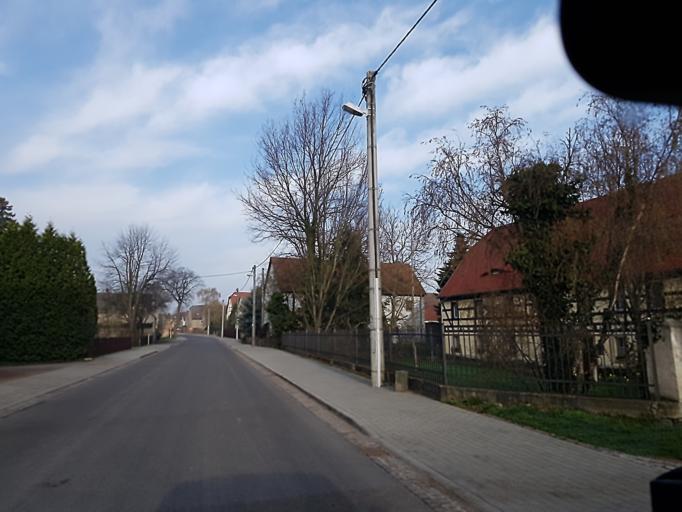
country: DE
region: Saxony
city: Naundorf
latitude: 51.2569
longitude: 13.1401
